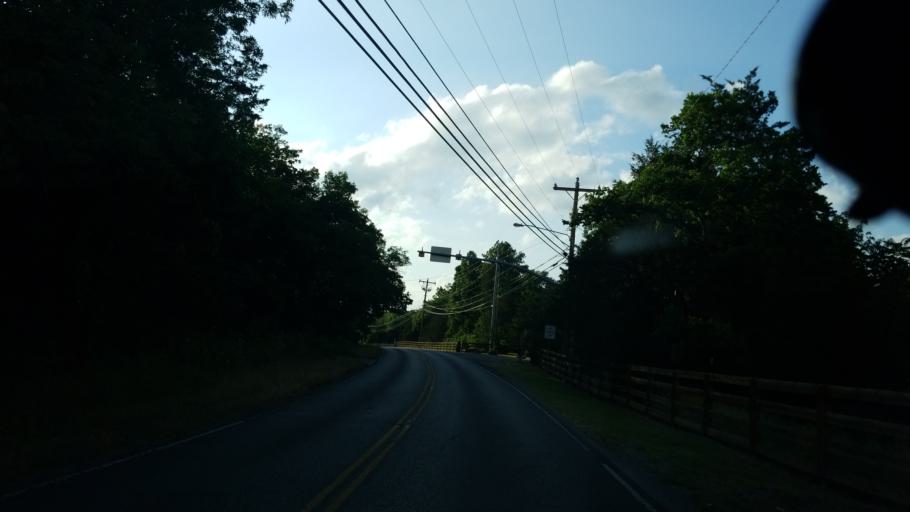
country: US
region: Tennessee
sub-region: Rutherford County
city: La Vergne
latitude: 36.0847
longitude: -86.5976
